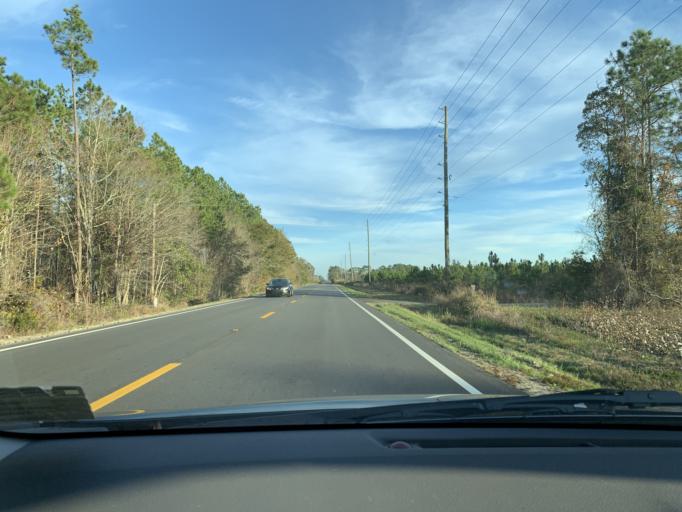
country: US
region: Georgia
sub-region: Irwin County
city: Ocilla
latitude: 31.5883
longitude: -83.0873
